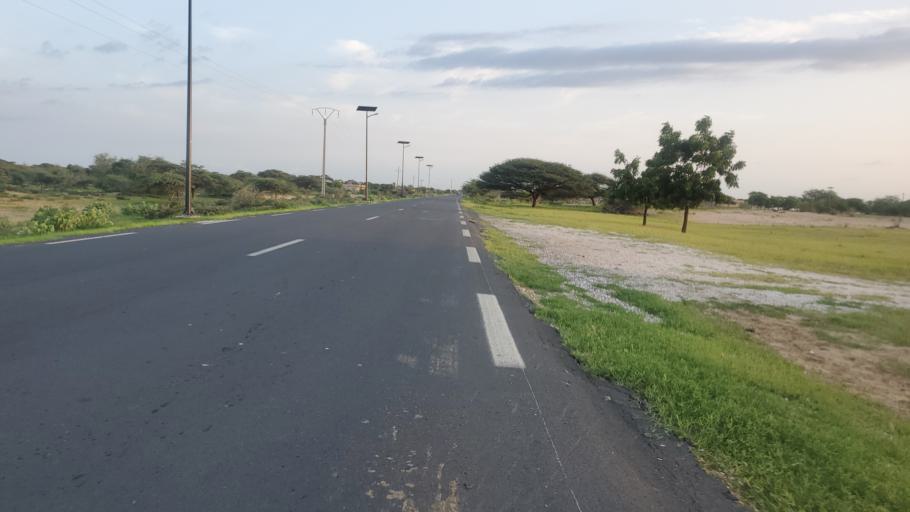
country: SN
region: Saint-Louis
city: Saint-Louis
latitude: 16.1461
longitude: -16.4097
